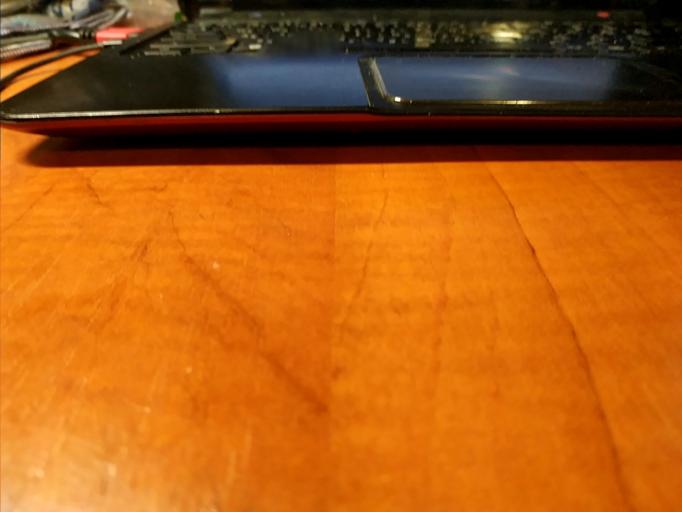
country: RU
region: Tverskaya
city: Ves'yegonsk
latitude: 58.7909
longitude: 37.5441
